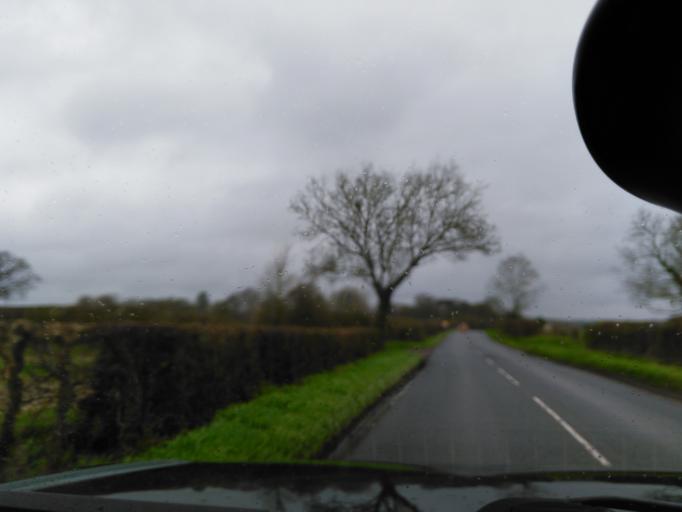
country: GB
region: England
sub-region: Wiltshire
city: Wingfield
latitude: 51.3224
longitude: -2.2578
